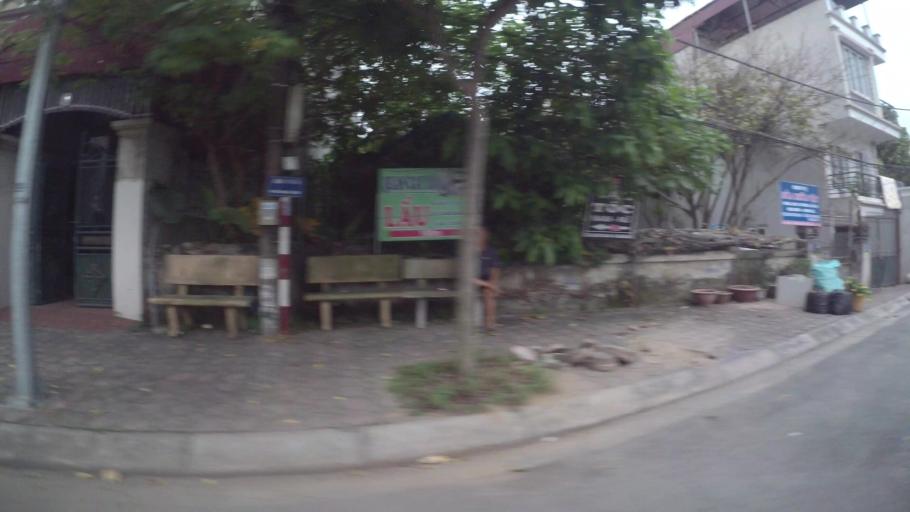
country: VN
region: Ha Noi
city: Trau Quy
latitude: 21.0537
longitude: 105.8991
